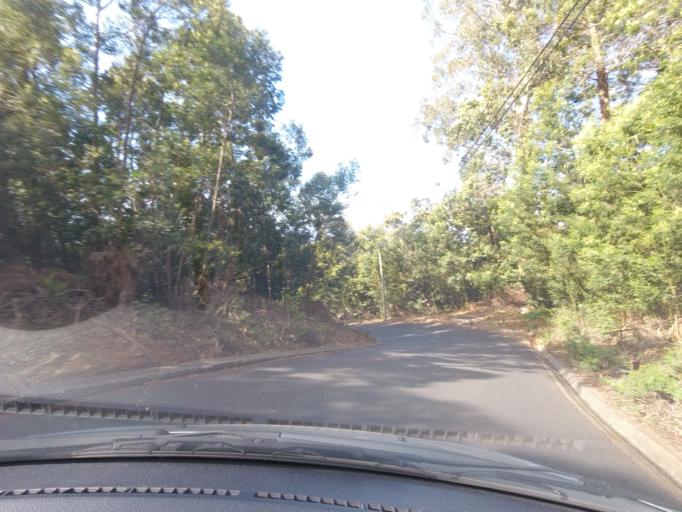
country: PT
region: Madeira
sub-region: Santa Cruz
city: Camacha
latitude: 32.6619
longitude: -16.8488
